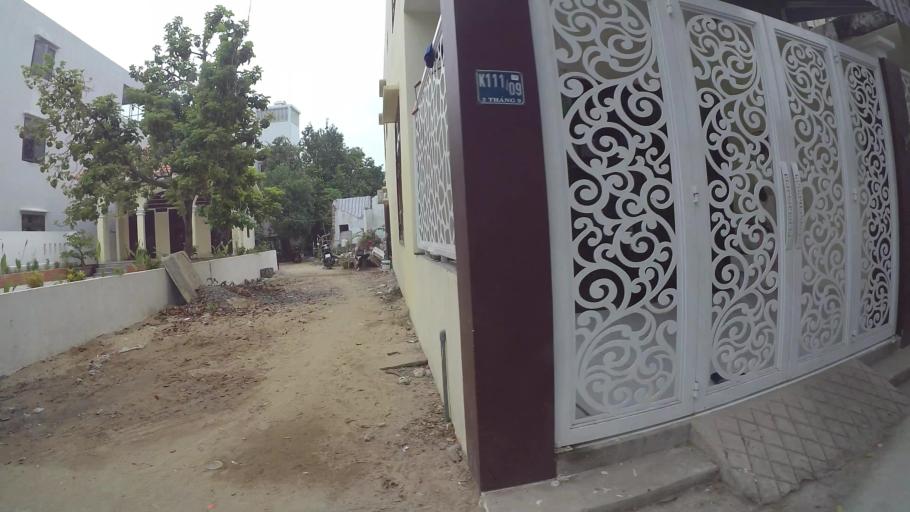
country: VN
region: Da Nang
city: Cam Le
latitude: 16.0281
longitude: 108.2233
